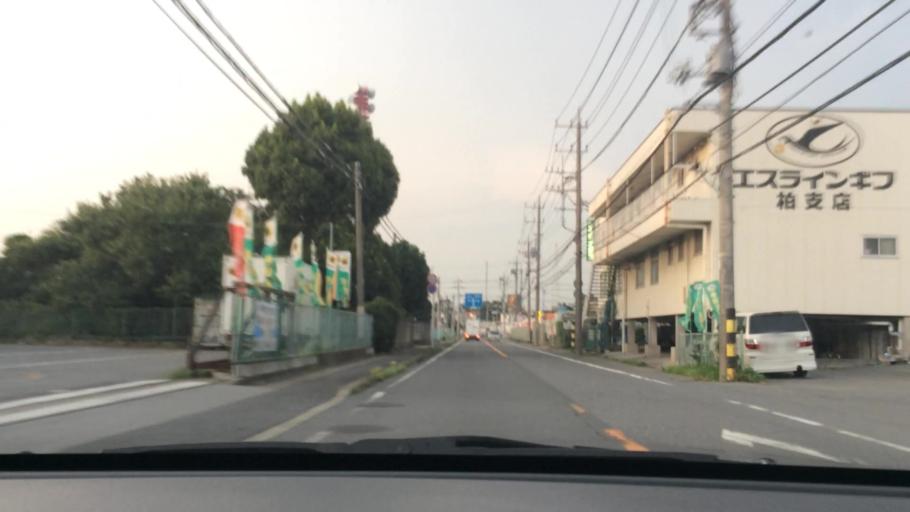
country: JP
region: Chiba
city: Kashiwa
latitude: 35.8856
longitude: 139.9377
